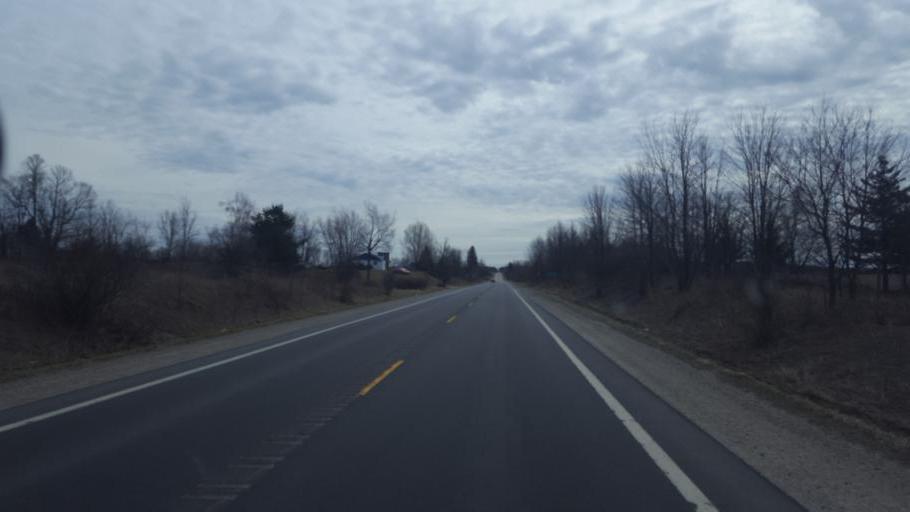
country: US
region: Michigan
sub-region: Isabella County
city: Lake Isabella
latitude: 43.7144
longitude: -85.1467
